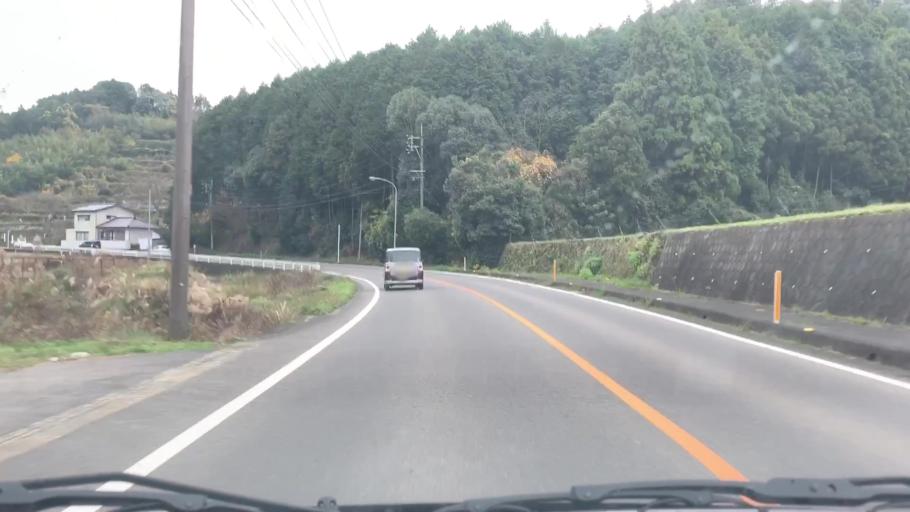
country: JP
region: Saga Prefecture
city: Ureshinomachi-shimojuku
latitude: 33.0907
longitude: 130.0078
